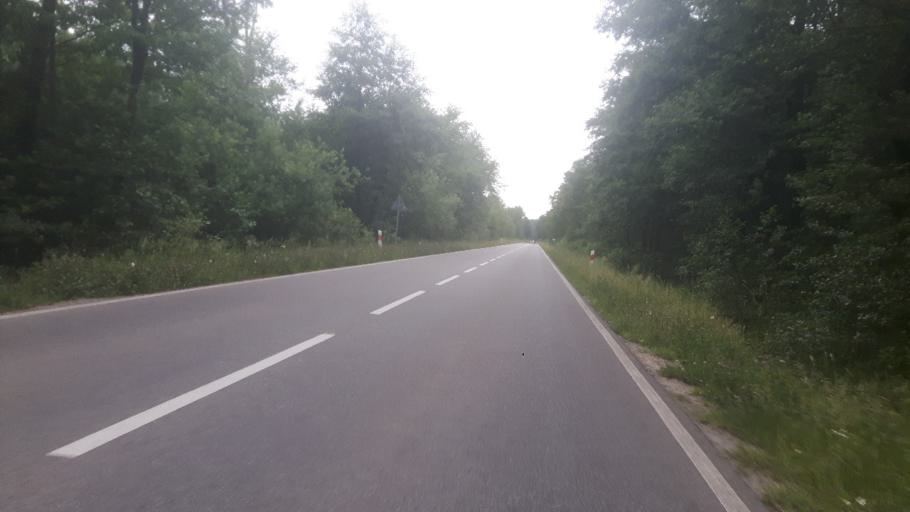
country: PL
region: Warmian-Masurian Voivodeship
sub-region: Powiat elblaski
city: Elblag
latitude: 54.2367
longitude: 19.3930
